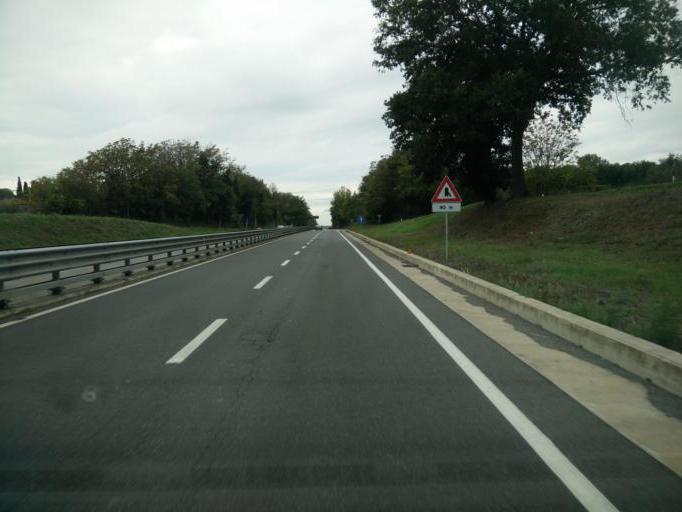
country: IT
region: Tuscany
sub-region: Provincia di Siena
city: Staggia
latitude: 43.4149
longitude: 11.1600
